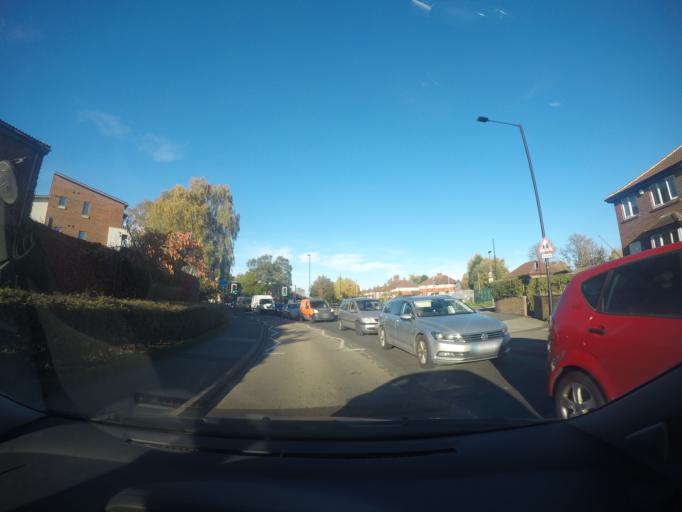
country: GB
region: England
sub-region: City of York
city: York
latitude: 53.9709
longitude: -1.0954
